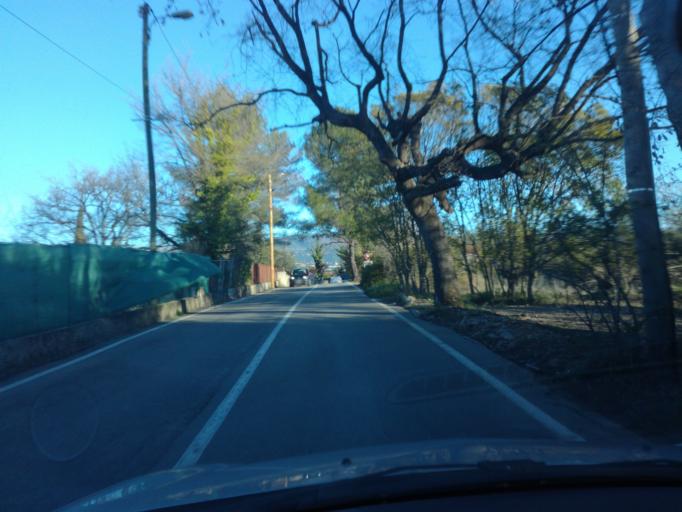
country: FR
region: Provence-Alpes-Cote d'Azur
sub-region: Departement des Alpes-Maritimes
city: La Roquette-sur-Siagne
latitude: 43.6096
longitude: 6.9668
